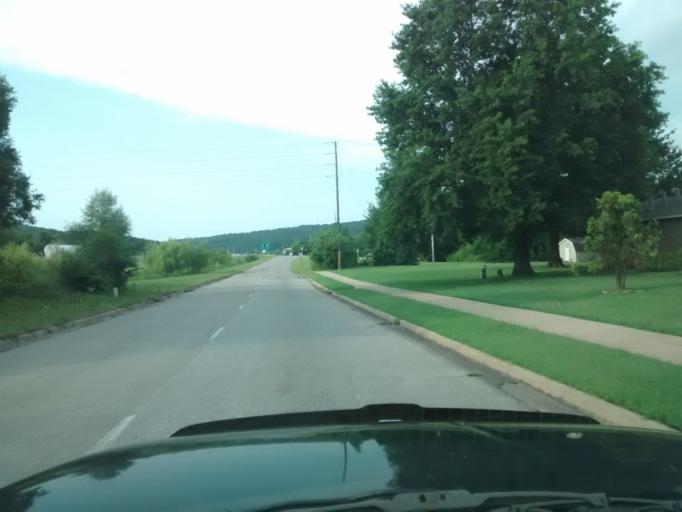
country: US
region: Arkansas
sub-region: Washington County
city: Fayetteville
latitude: 36.0764
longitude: -94.2026
